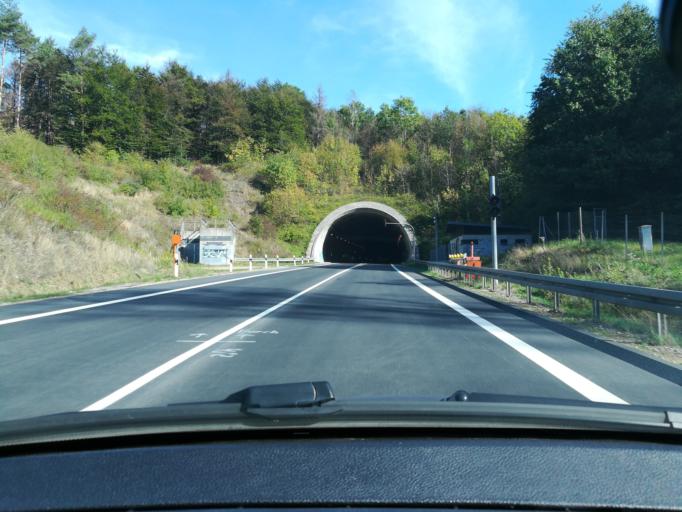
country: DE
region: North Rhine-Westphalia
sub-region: Regierungsbezirk Detmold
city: Oerlinghausen
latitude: 51.9536
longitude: 8.6485
